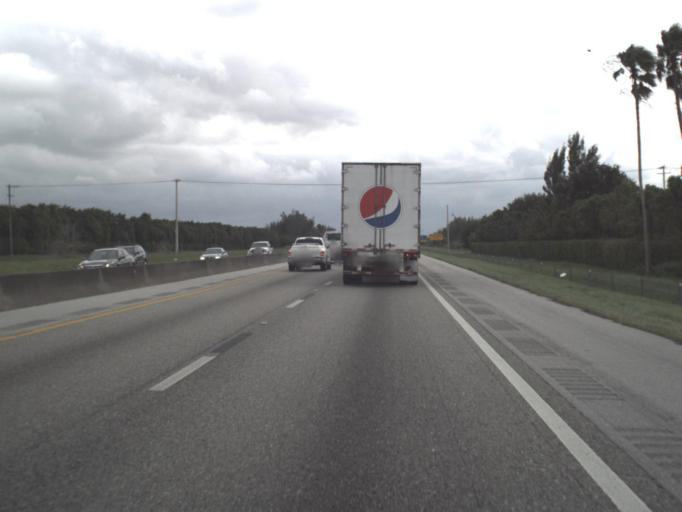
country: US
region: Florida
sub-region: Palm Beach County
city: Greenacres City
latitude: 26.5820
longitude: -80.1734
